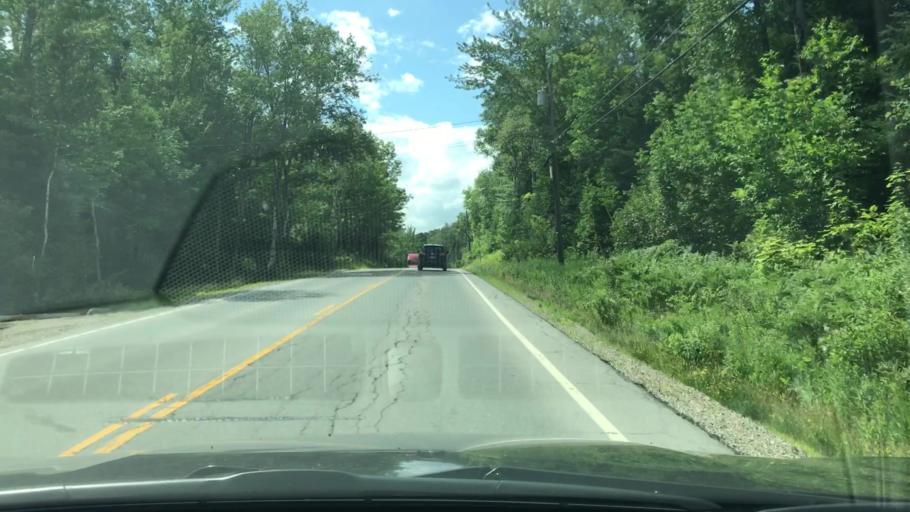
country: US
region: New Hampshire
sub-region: Coos County
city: Jefferson
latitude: 44.3608
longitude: -71.3753
